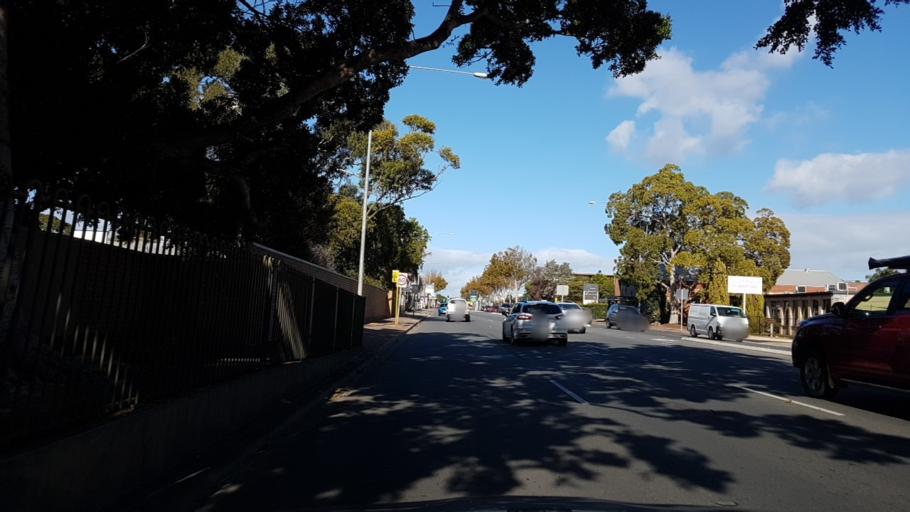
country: AU
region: South Australia
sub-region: Unley
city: Forestville
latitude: -34.9434
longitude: 138.5712
